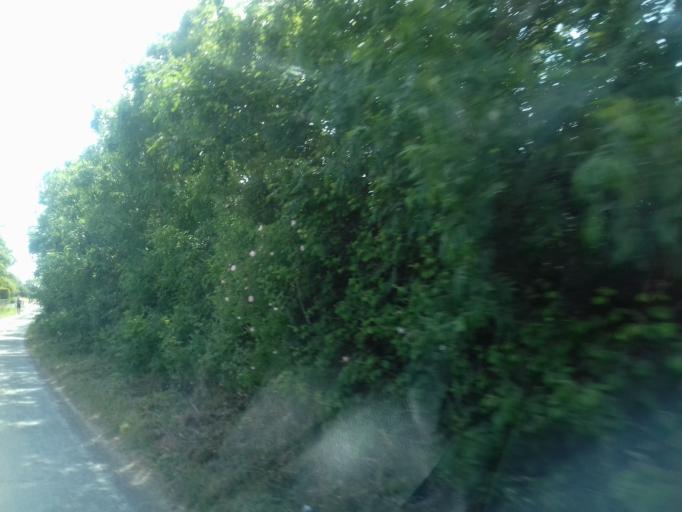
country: IE
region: Leinster
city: Lusk
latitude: 53.5281
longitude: -6.1394
